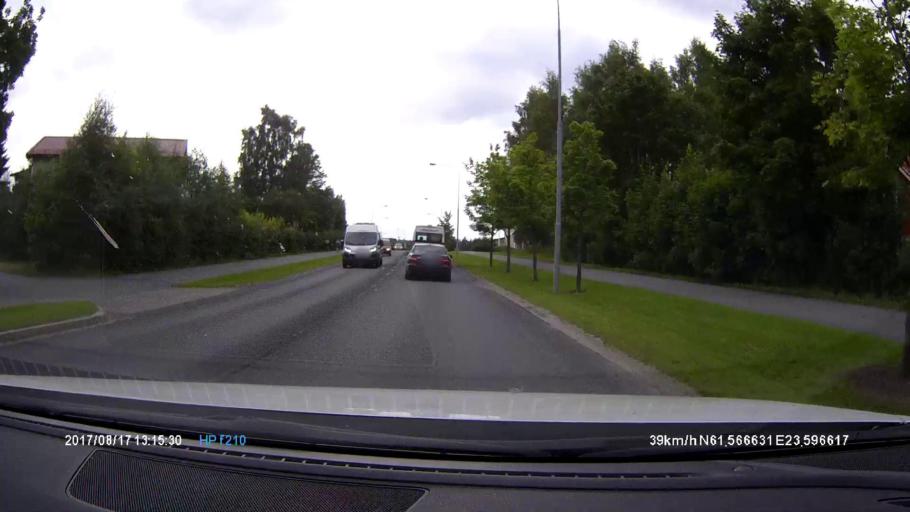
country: FI
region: Pirkanmaa
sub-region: Tampere
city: Yloejaervi
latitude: 61.5665
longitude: 23.5965
